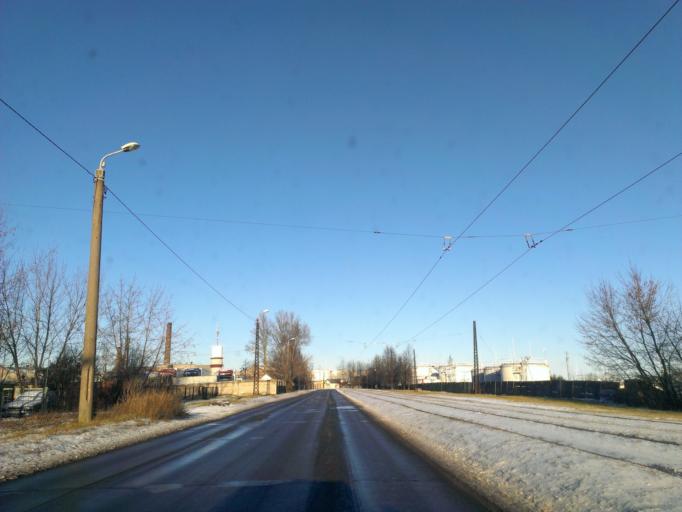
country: LV
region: Riga
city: Jaunciems
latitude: 57.0129
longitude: 24.1245
